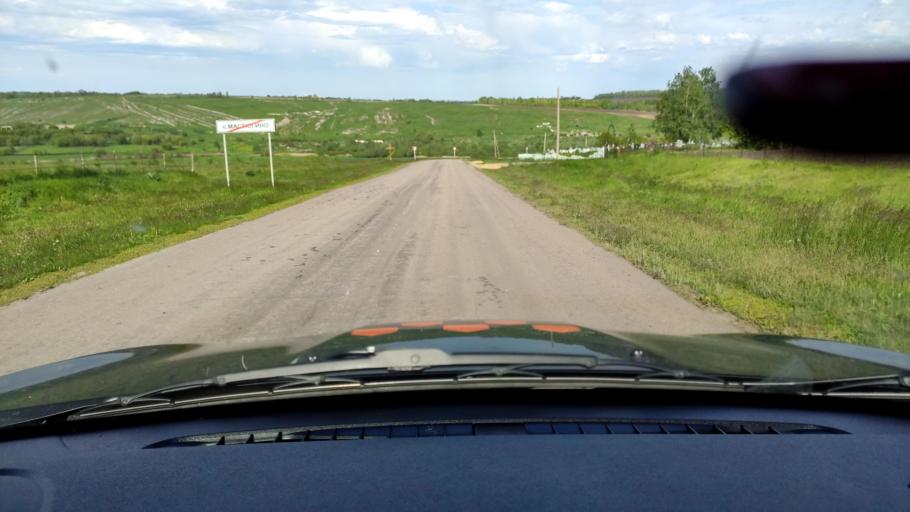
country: RU
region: Voronezj
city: Uryv-Pokrovka
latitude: 51.2006
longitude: 39.0473
